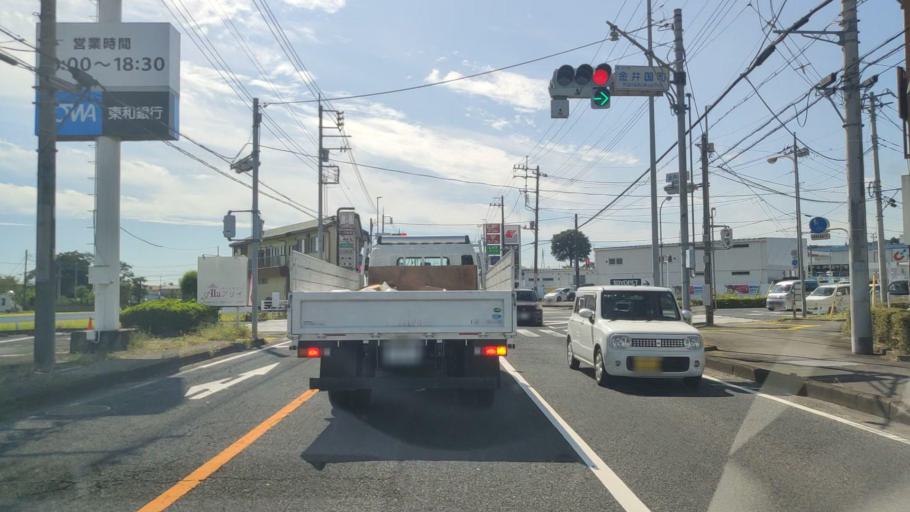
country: JP
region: Gunma
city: Shibukawa
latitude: 36.5102
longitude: 139.0053
